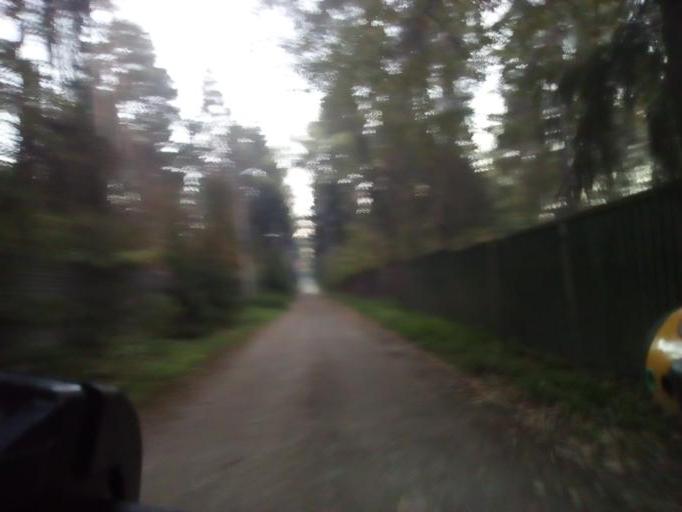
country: RU
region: Moskovskaya
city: Kratovo
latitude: 55.6073
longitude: 38.1591
